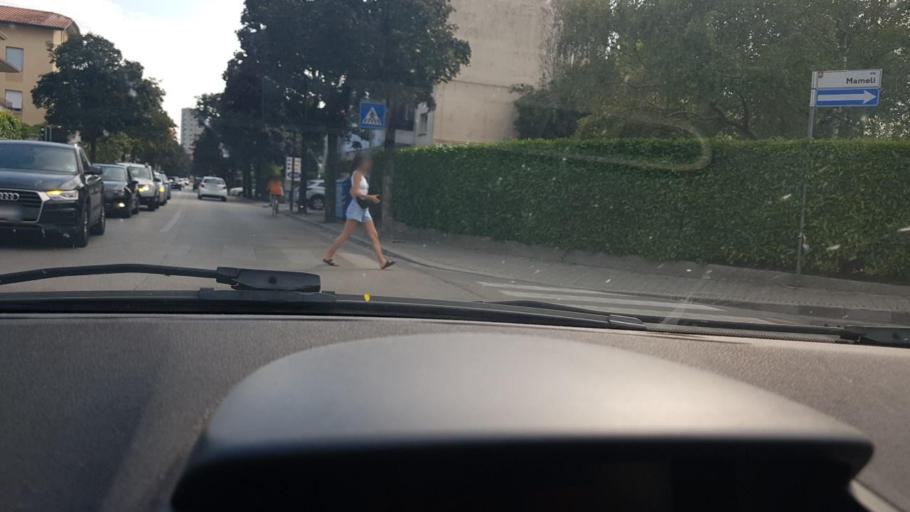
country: IT
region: Friuli Venezia Giulia
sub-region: Provincia di Pordenone
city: Pordenone
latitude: 45.9630
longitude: 12.6688
